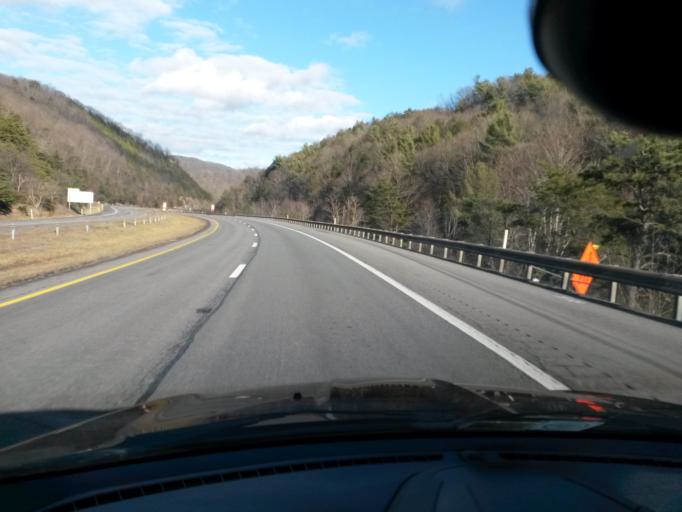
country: US
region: West Virginia
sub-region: Mercer County
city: Princeton
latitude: 37.2959
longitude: -81.1035
